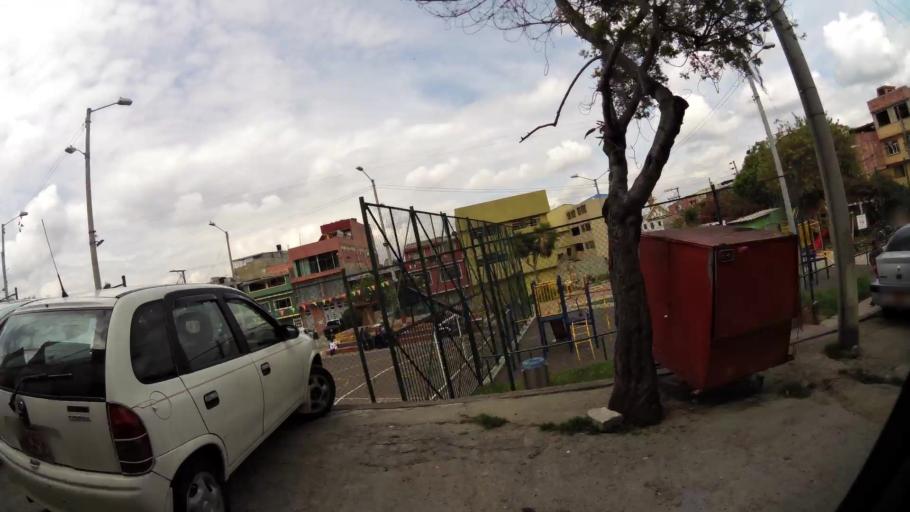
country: CO
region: Cundinamarca
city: La Calera
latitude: 4.7484
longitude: -74.0221
